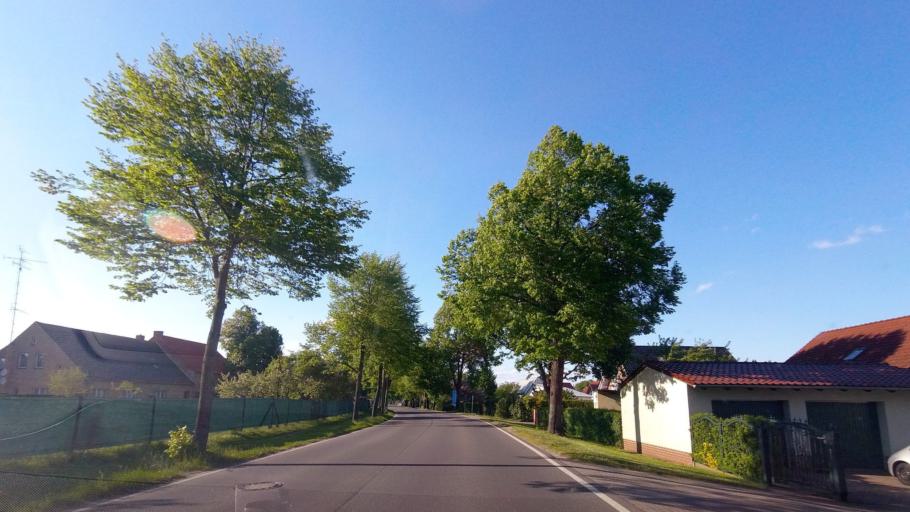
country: DE
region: Brandenburg
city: Luebben
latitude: 51.9267
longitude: 13.8958
